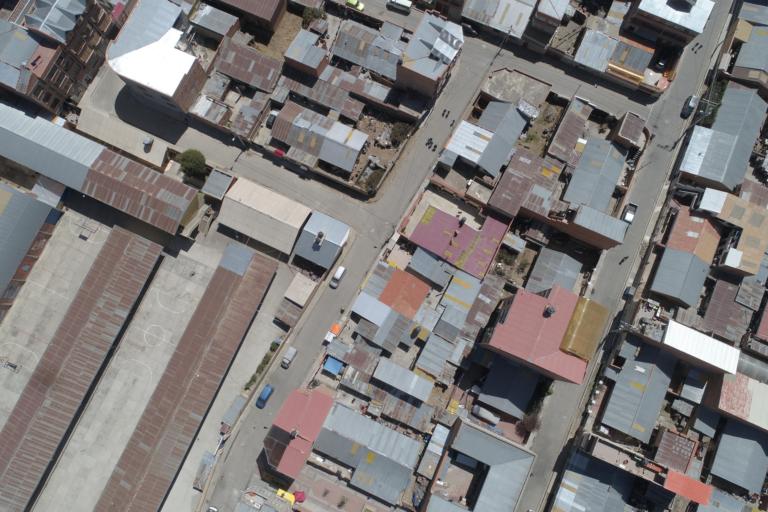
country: BO
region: La Paz
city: La Paz
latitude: -16.5206
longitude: -68.1531
